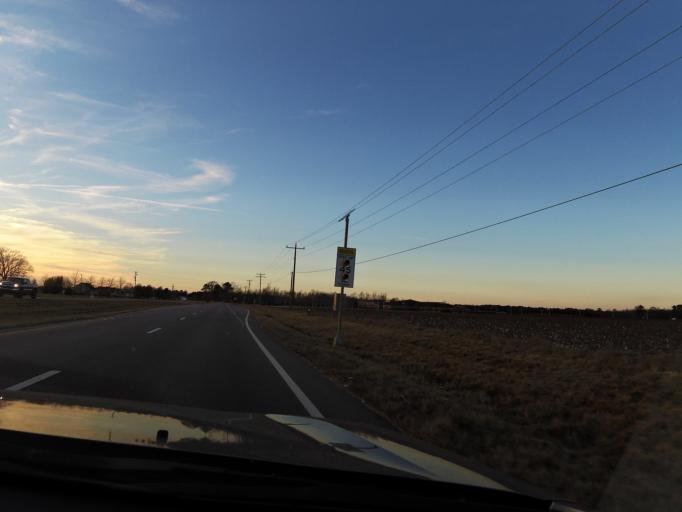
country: US
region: Virginia
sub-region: City of Franklin
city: Franklin
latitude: 36.6883
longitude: -76.9770
